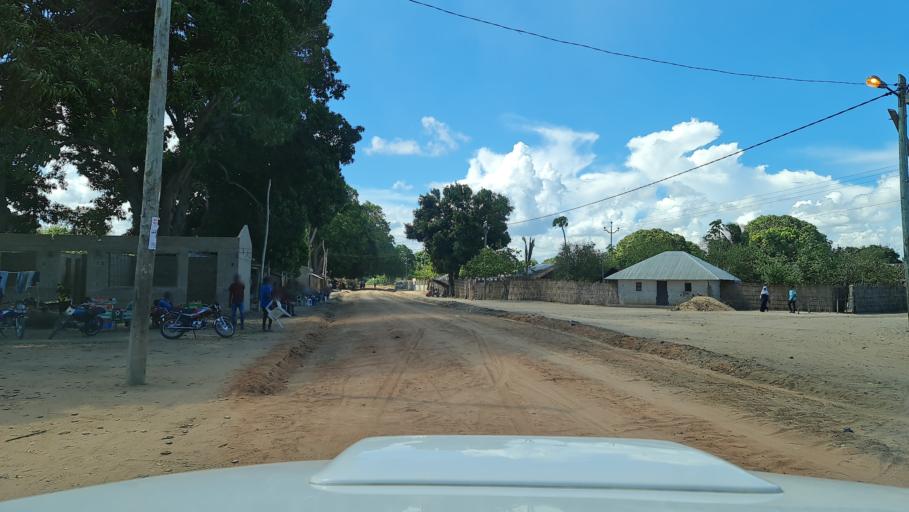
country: MZ
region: Nampula
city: Ilha de Mocambique
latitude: -15.5484
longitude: 40.4047
